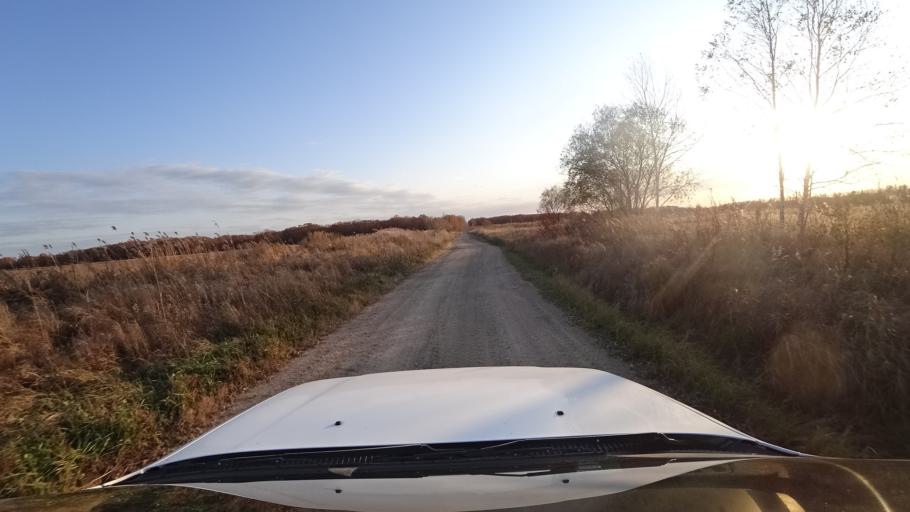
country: RU
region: Primorskiy
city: Lazo
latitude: 45.8094
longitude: 133.6072
